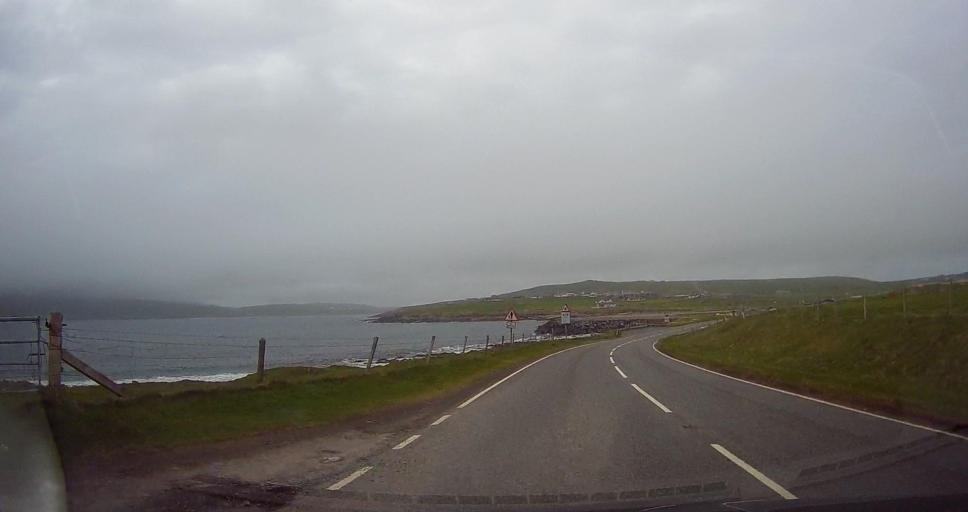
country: GB
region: Scotland
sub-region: Shetland Islands
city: Sandwick
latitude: 59.8774
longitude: -1.3069
